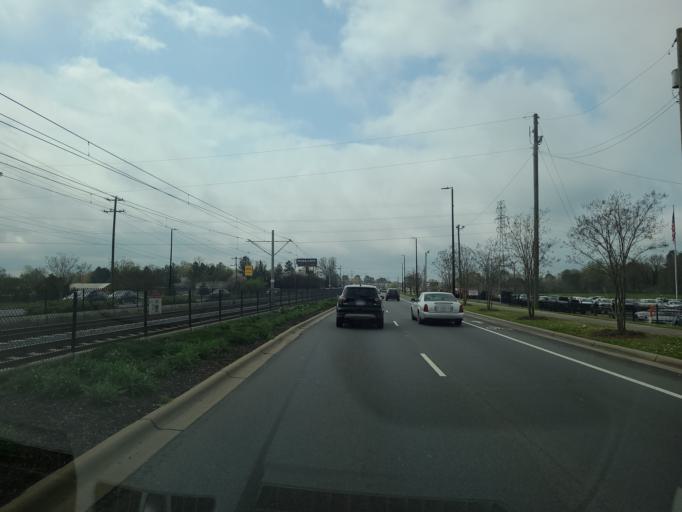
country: US
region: North Carolina
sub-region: Mecklenburg County
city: Charlotte
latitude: 35.2701
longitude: -80.7679
